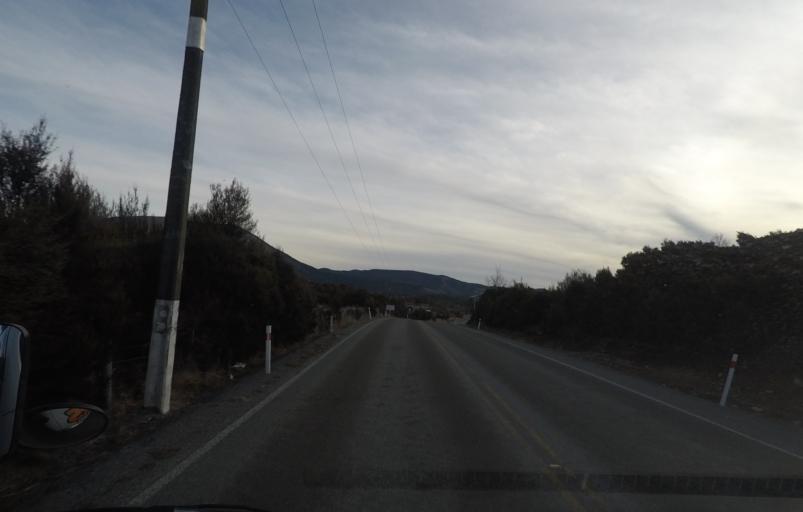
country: NZ
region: Tasman
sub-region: Tasman District
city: Wakefield
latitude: -41.8005
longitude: 172.8597
